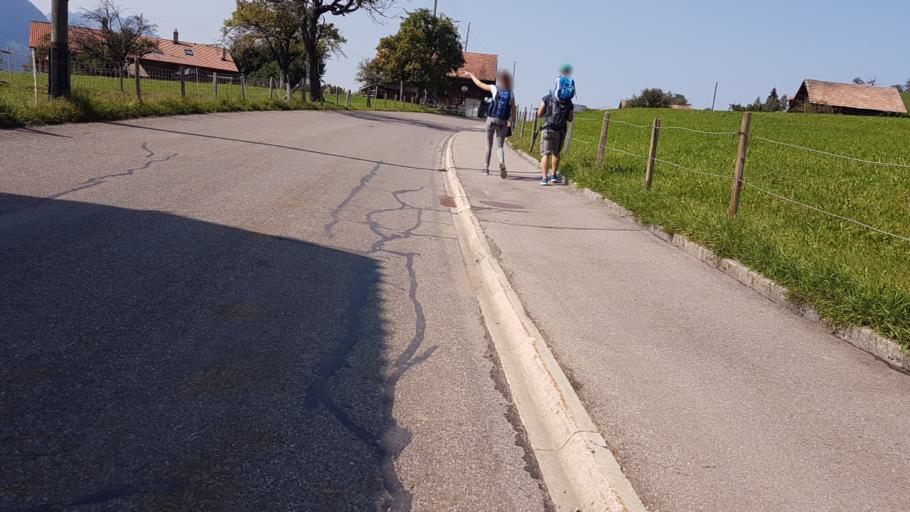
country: CH
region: Bern
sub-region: Frutigen-Niedersimmental District
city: Aeschi
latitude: 46.6406
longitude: 7.7307
